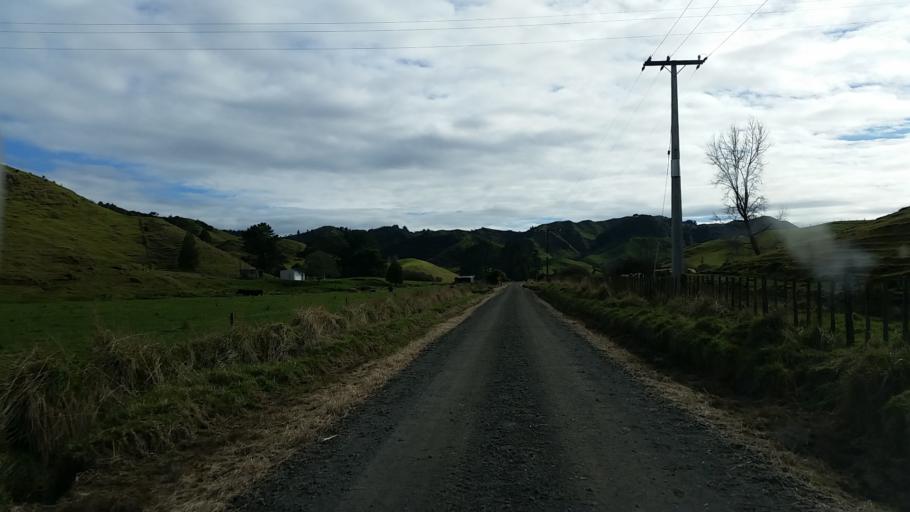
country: NZ
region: Taranaki
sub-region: South Taranaki District
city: Eltham
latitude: -39.2323
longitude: 174.5673
